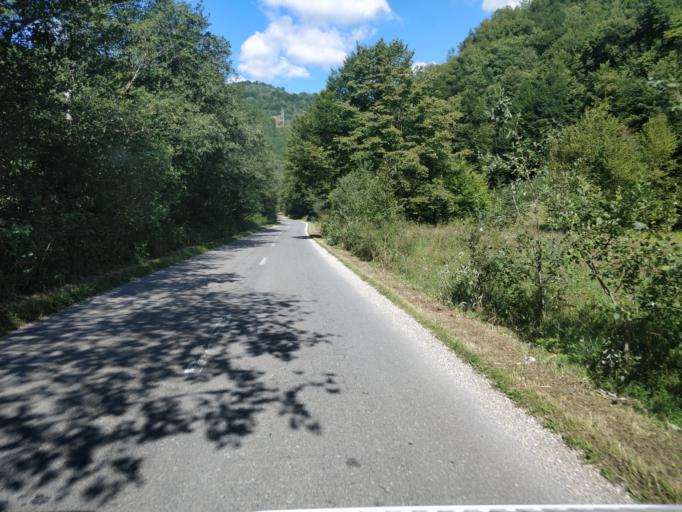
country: RO
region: Cluj
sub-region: Comuna Sacueu
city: Sacuieu
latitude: 46.8324
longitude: 22.8659
